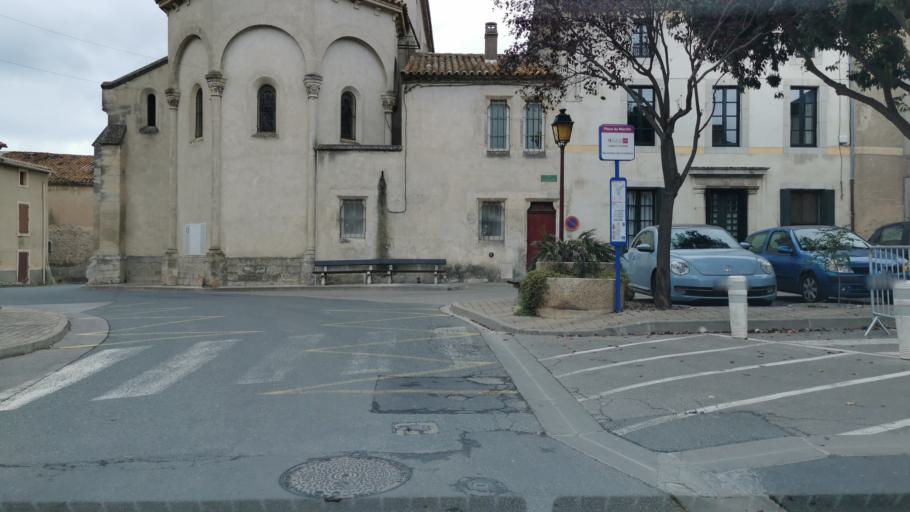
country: FR
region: Languedoc-Roussillon
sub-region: Departement de l'Aude
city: Nevian
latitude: 43.1915
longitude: 2.9272
